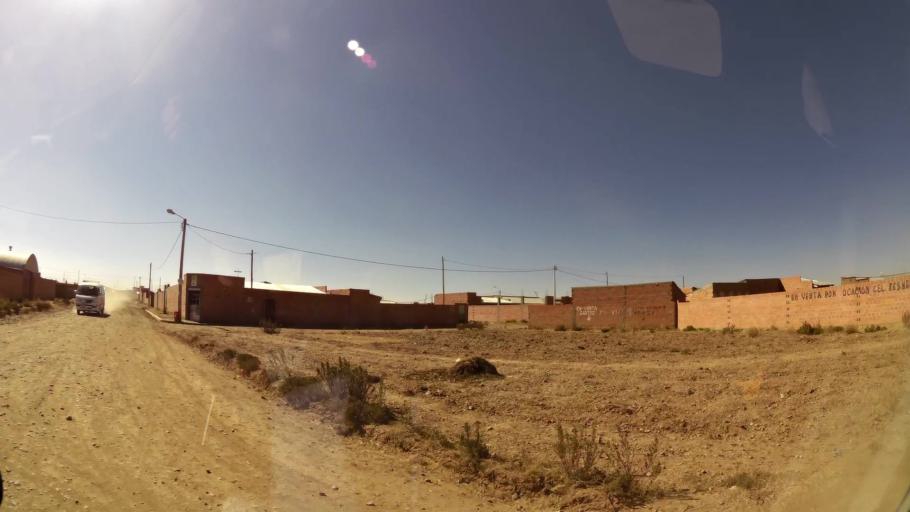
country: BO
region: La Paz
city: La Paz
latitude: -16.6248
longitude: -68.1954
